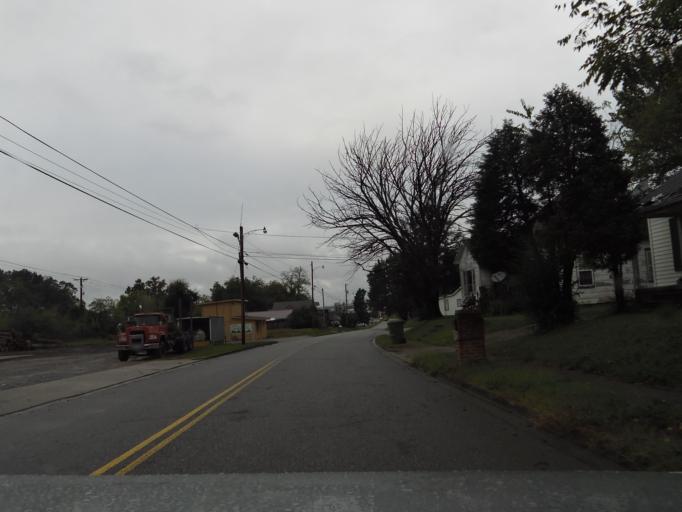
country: US
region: Tennessee
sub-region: Blount County
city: Maryville
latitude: 35.7670
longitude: -83.9656
